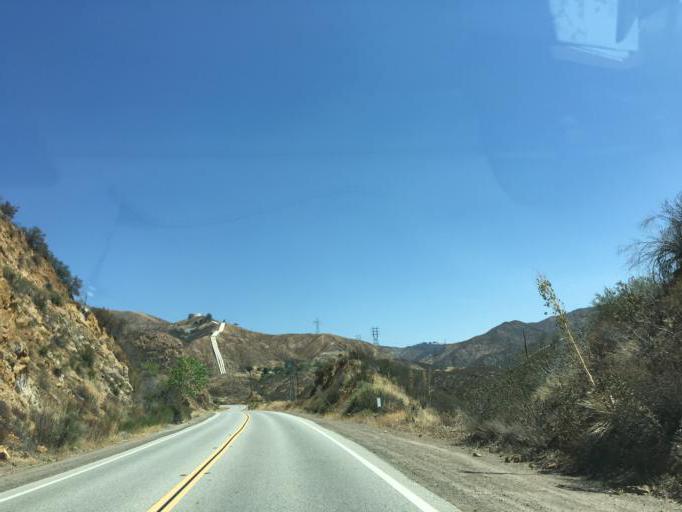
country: US
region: California
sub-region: Los Angeles County
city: Green Valley
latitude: 34.5848
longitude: -118.4560
